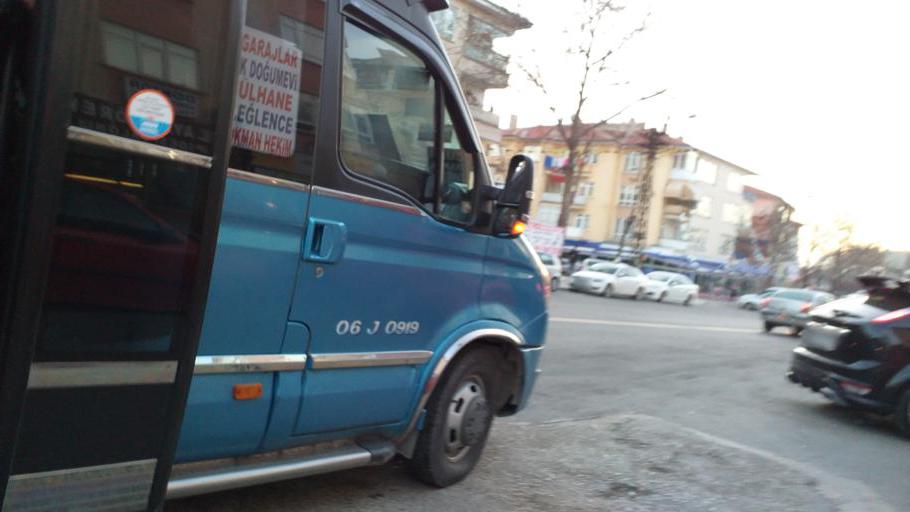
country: TR
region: Ankara
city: Ankara
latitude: 39.9797
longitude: 32.8366
